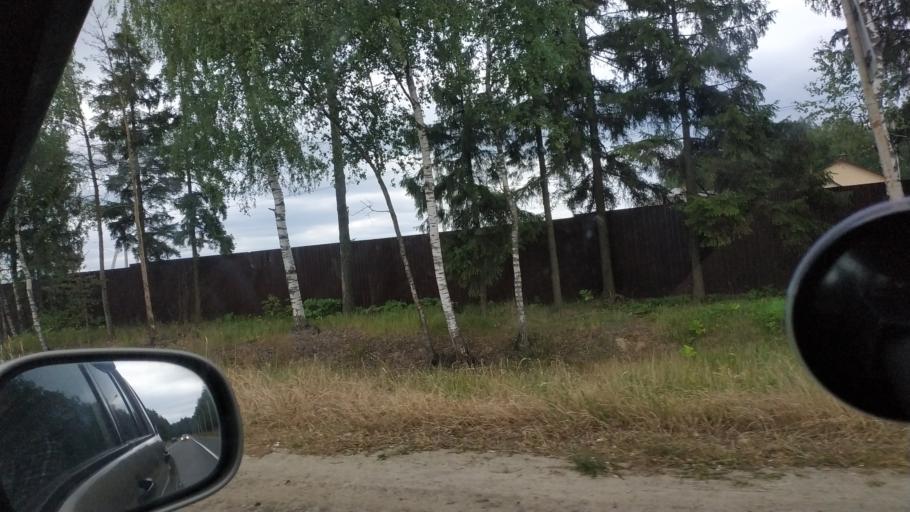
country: RU
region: Moskovskaya
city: Krasnoarmeysk
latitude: 56.0511
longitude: 38.2280
